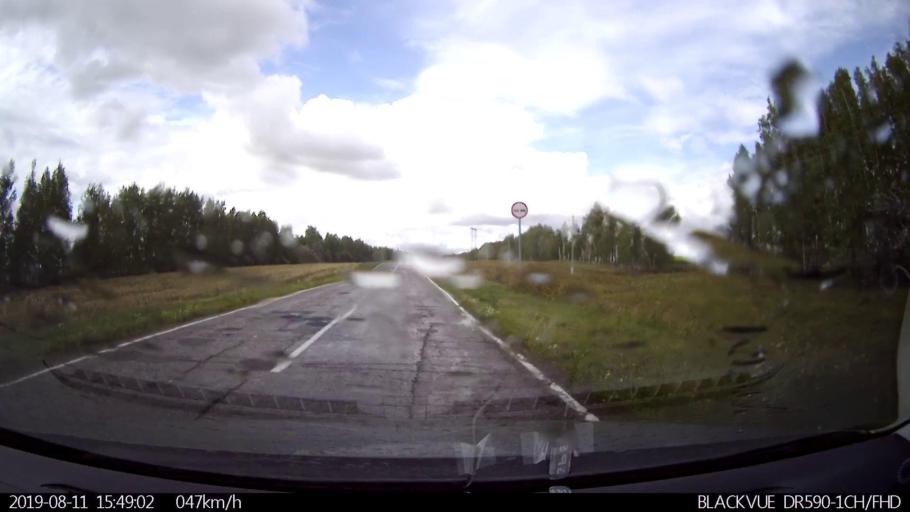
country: RU
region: Ulyanovsk
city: Ignatovka
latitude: 53.9012
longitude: 47.6547
